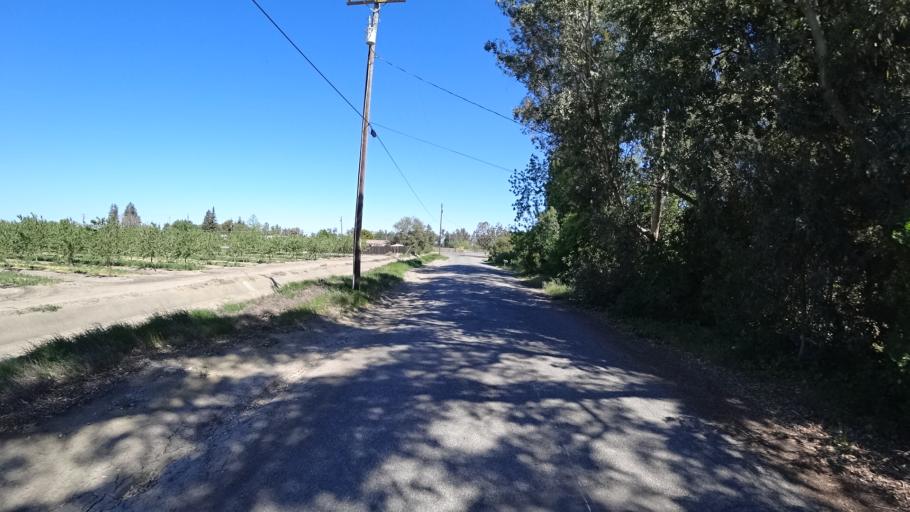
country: US
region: California
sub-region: Glenn County
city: Orland
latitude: 39.7457
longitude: -122.1276
